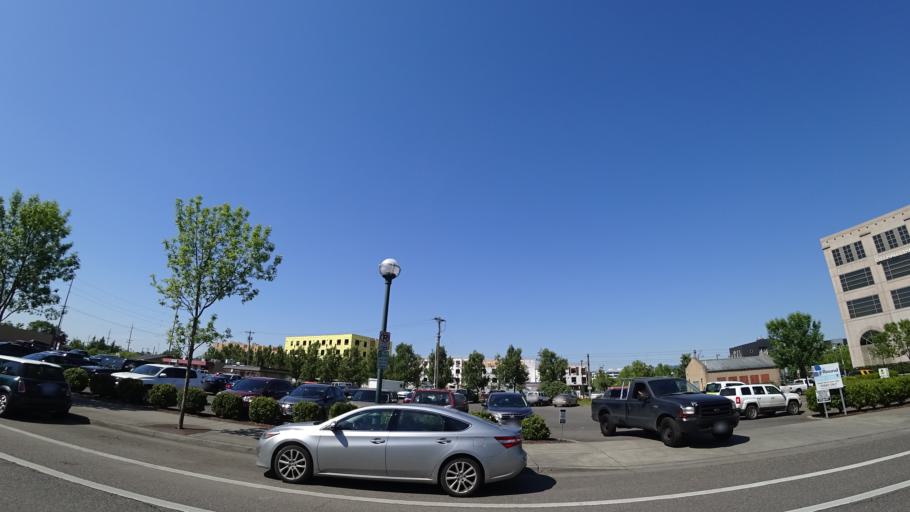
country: US
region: Oregon
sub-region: Washington County
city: Beaverton
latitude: 45.4897
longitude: -122.8090
